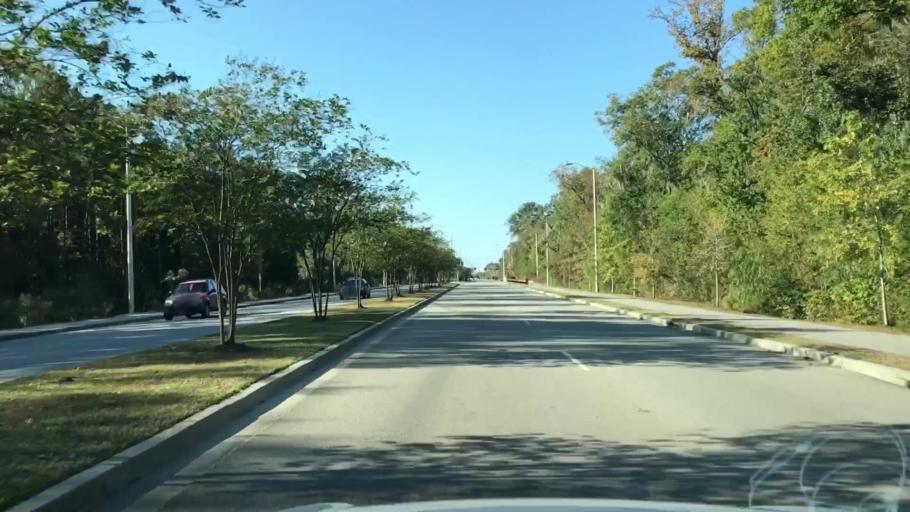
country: US
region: South Carolina
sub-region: Charleston County
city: Shell Point
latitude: 32.8110
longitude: -80.1075
